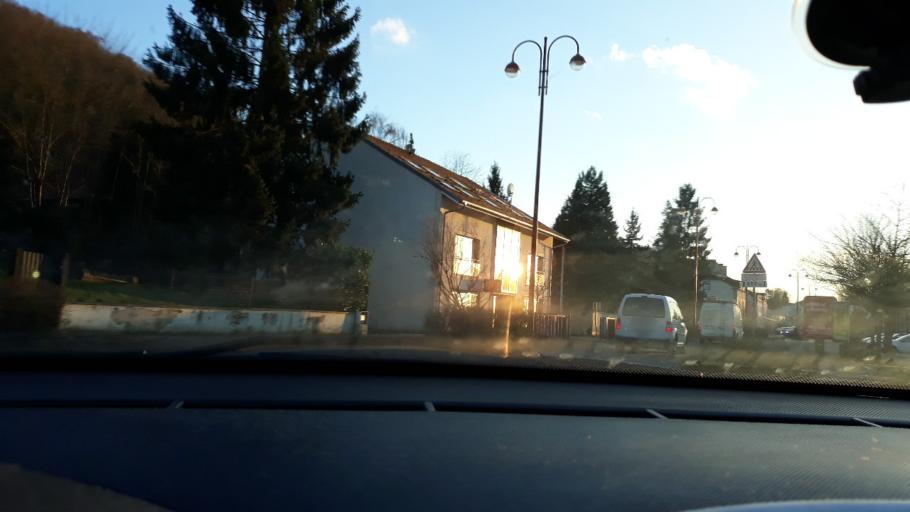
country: FR
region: Lorraine
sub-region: Departement de la Moselle
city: Spicheren
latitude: 49.2044
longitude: 6.9558
